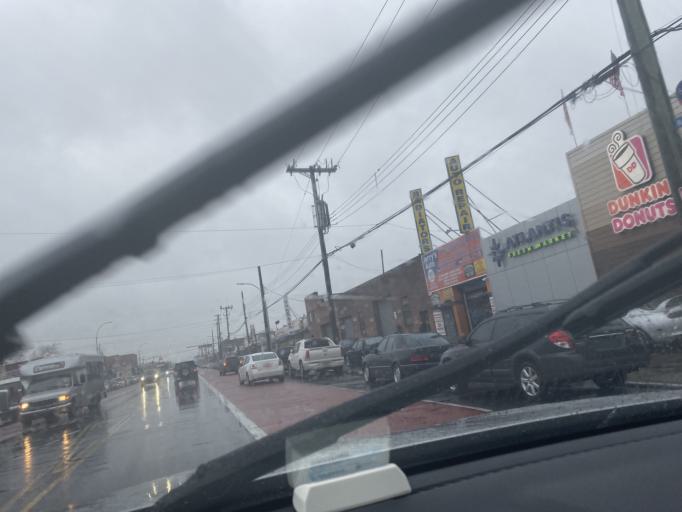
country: US
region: New York
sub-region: Kings County
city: Brooklyn
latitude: 40.6448
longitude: -73.9297
